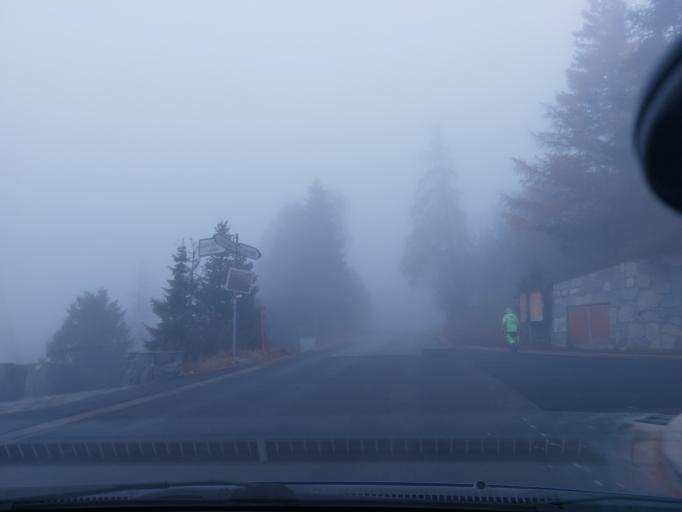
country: CH
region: Valais
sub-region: Sierre District
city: Lens
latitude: 46.2986
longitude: 7.4507
